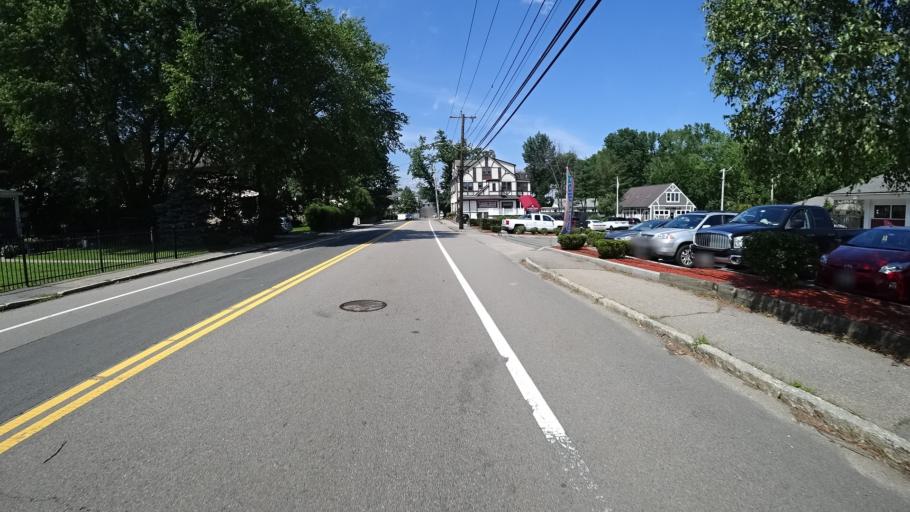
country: US
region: Massachusetts
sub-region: Norfolk County
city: Dedham
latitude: 42.2666
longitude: -71.1766
